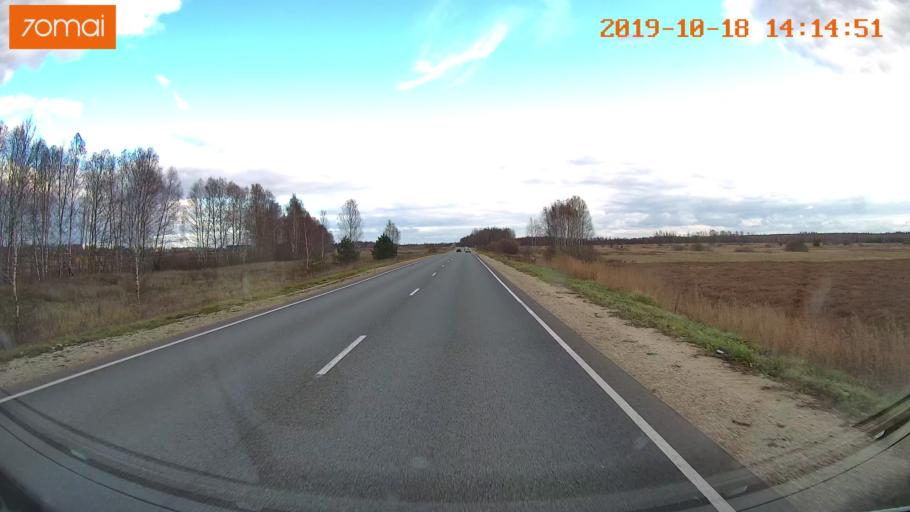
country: RU
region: Rjazan
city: Spas-Klepiki
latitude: 55.1481
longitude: 40.3047
